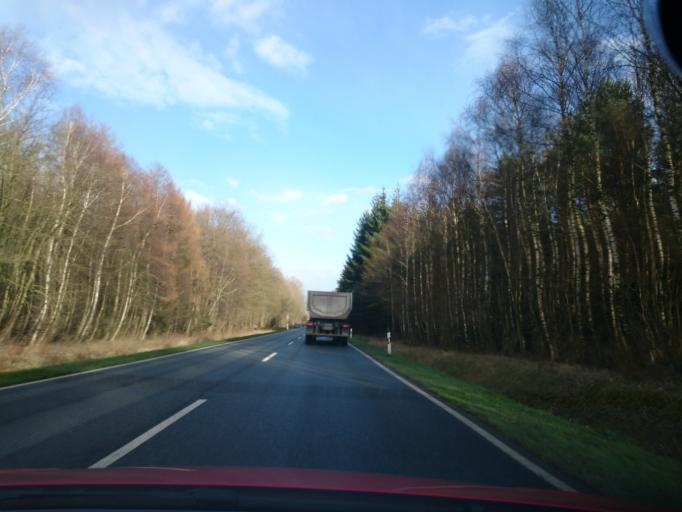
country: DE
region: Mecklenburg-Vorpommern
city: Velgast
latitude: 54.2996
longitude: 12.8543
